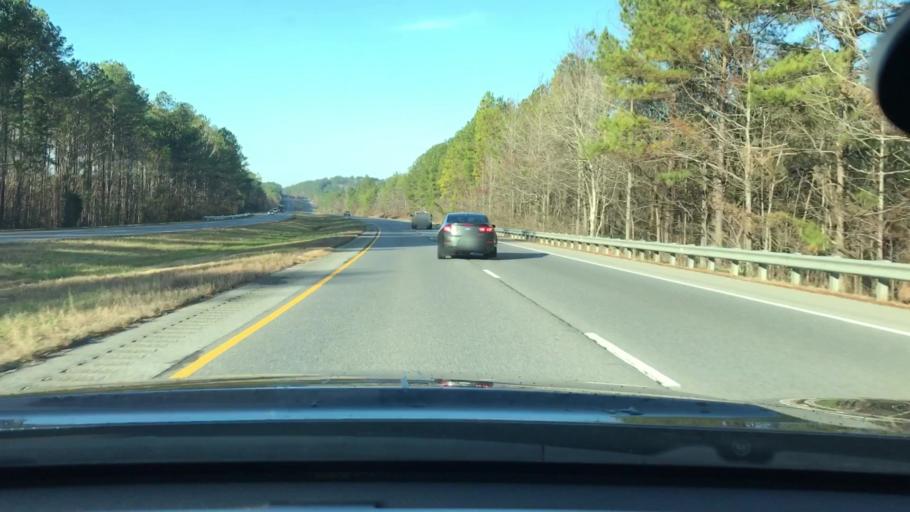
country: US
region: Alabama
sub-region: Shelby County
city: Westover
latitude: 33.3574
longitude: -86.4923
